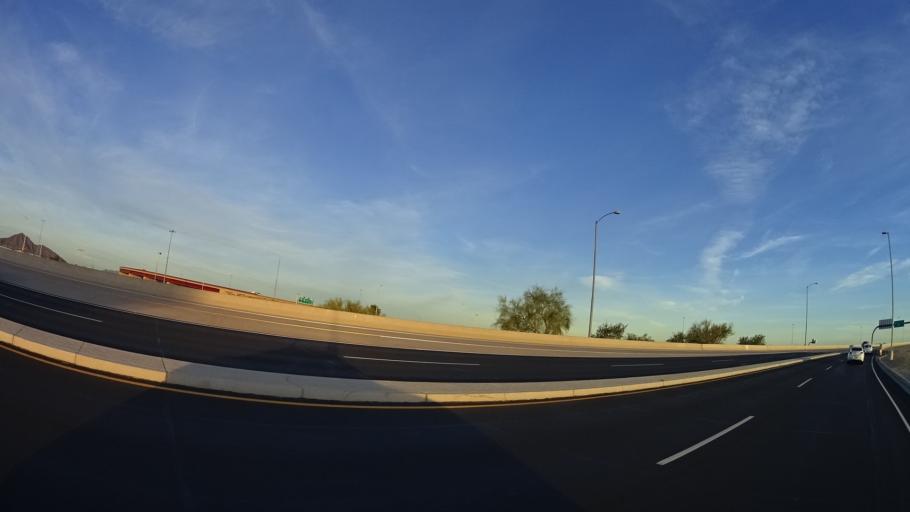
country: US
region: Arizona
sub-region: Maricopa County
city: Tempe Junction
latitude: 33.4350
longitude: -111.9808
